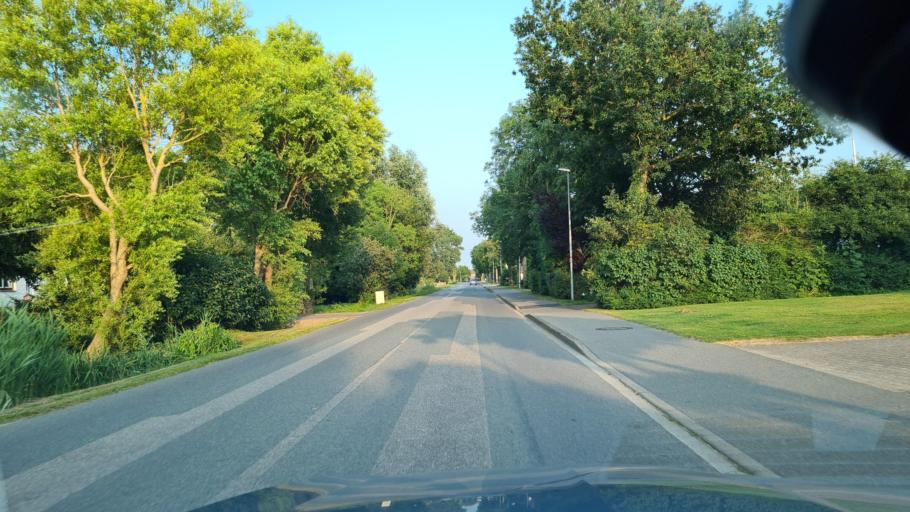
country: DE
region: Schleswig-Holstein
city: Elisabeth-Sophien-Koog
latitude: 54.4919
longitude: 8.8668
